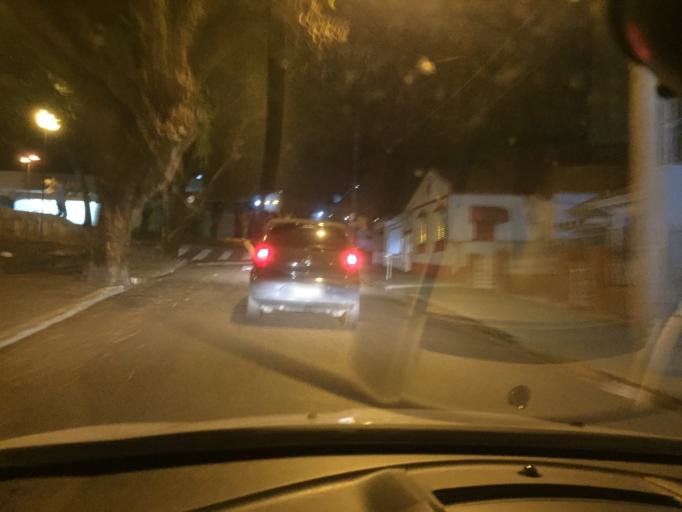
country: BR
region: Sao Paulo
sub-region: Jundiai
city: Jundiai
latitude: -23.2047
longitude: -46.8705
